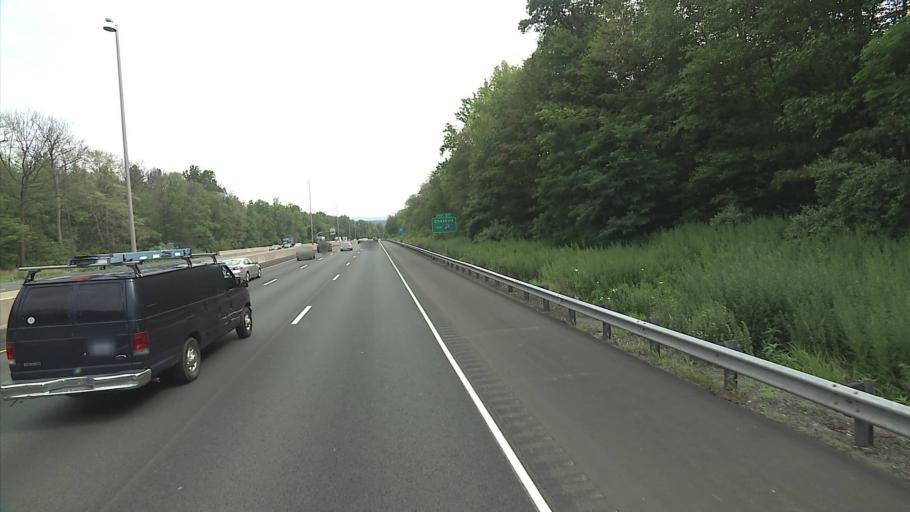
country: US
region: Connecticut
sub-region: New Haven County
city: Cheshire Village
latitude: 41.5500
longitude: -72.9359
